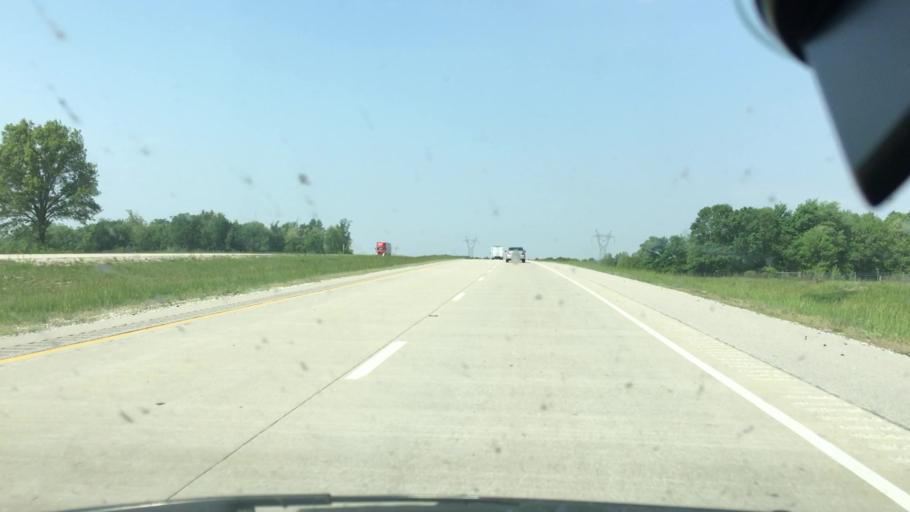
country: US
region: Indiana
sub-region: Daviess County
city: Washington
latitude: 38.6213
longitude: -87.1560
